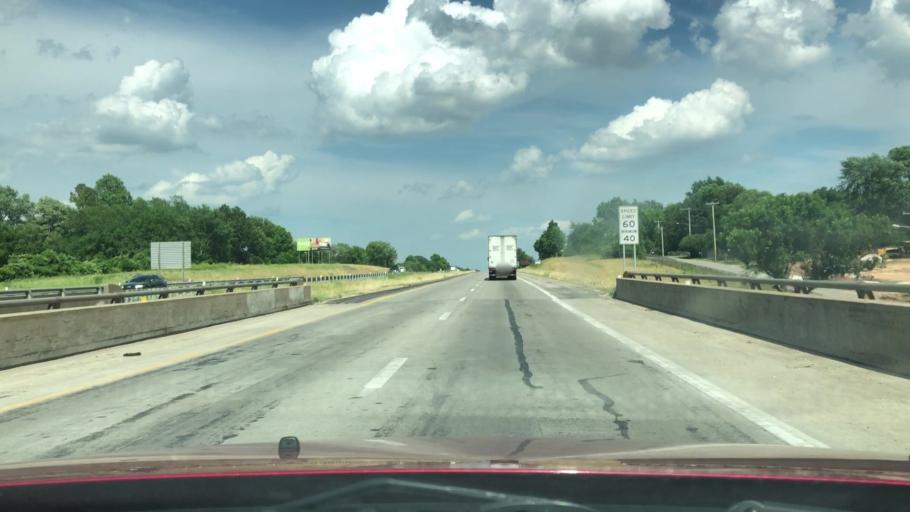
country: US
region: Missouri
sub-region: Greene County
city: Springfield
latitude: 37.2502
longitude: -93.3018
